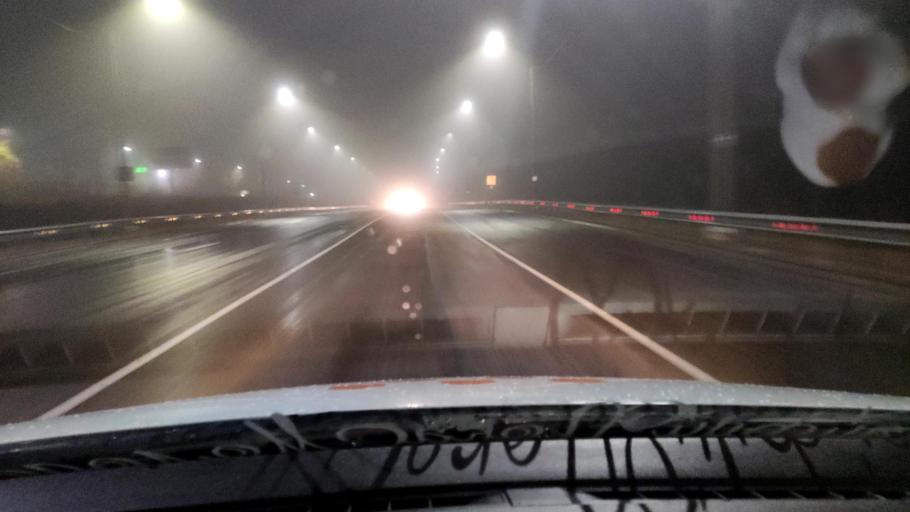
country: RU
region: Voronezj
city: Devitsa
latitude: 51.6330
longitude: 38.9642
